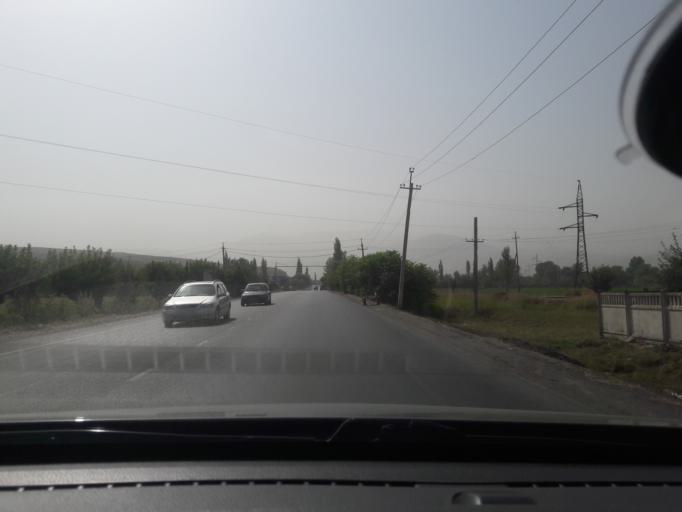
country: TJ
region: Republican Subordination
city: Vahdat
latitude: 38.5272
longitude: 69.0268
